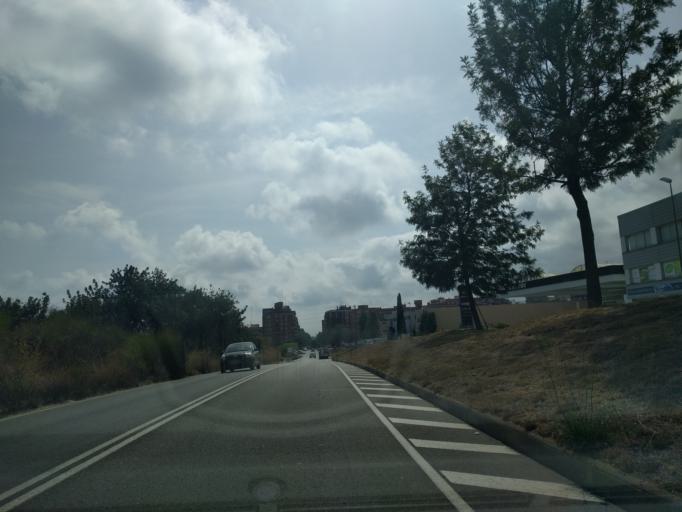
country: ES
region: Catalonia
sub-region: Provincia de Barcelona
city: Mataro
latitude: 41.5511
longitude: 2.4554
